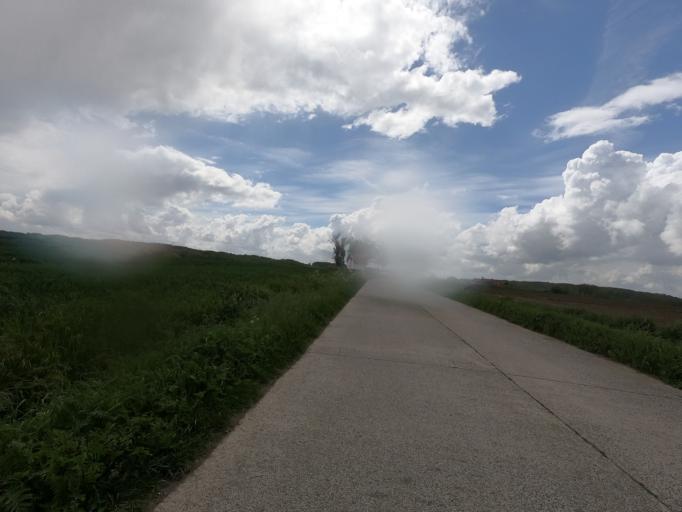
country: BE
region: Flanders
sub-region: Provincie Oost-Vlaanderen
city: Ronse
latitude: 50.7801
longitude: 3.5539
